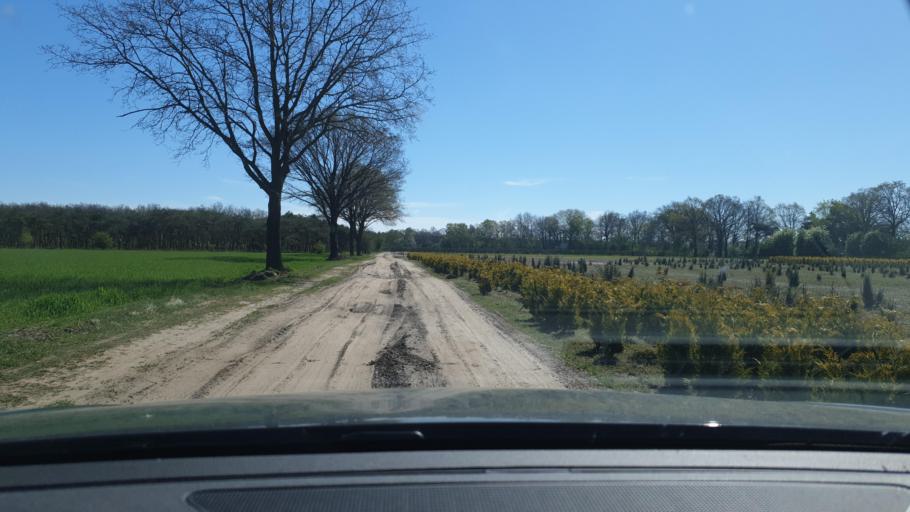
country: NL
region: Limburg
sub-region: Gemeente Venlo
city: Arcen
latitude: 51.4383
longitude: 6.1128
